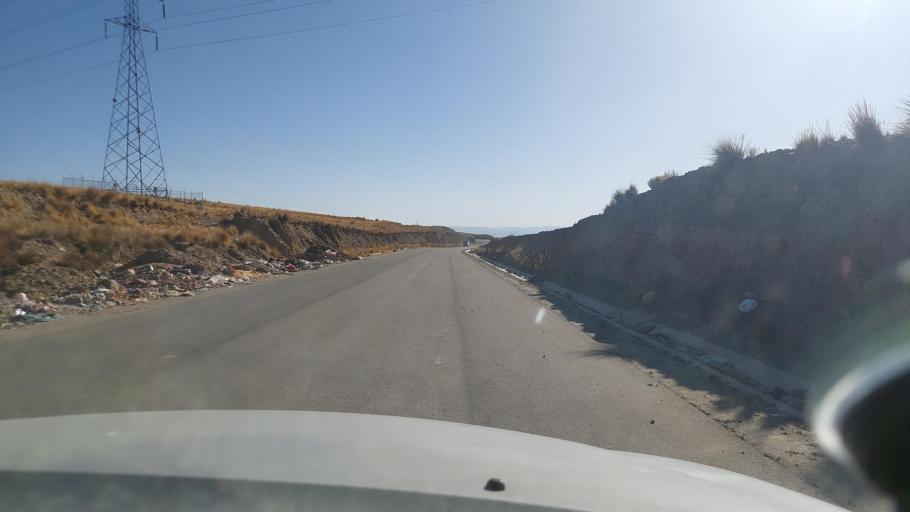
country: BO
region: La Paz
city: La Paz
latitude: -16.4338
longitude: -68.1592
